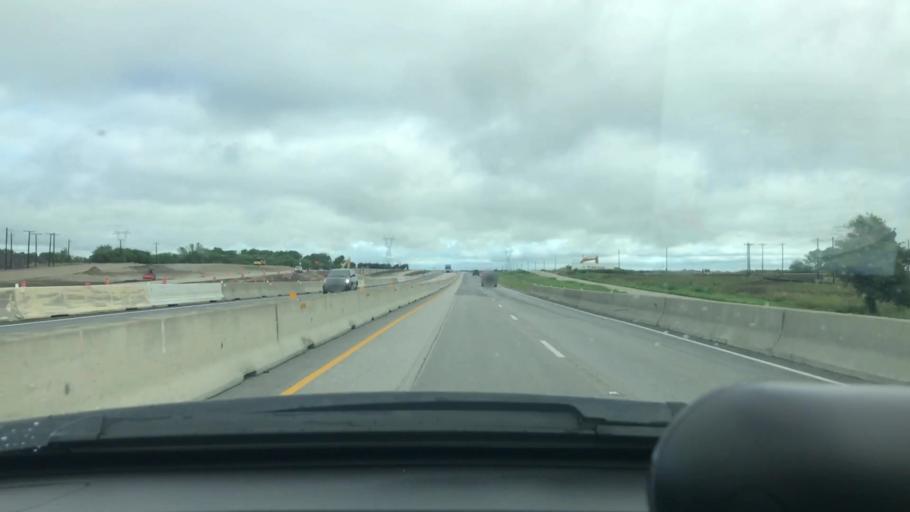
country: US
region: Texas
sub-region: Collin County
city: Anna
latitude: 33.3603
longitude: -96.5837
